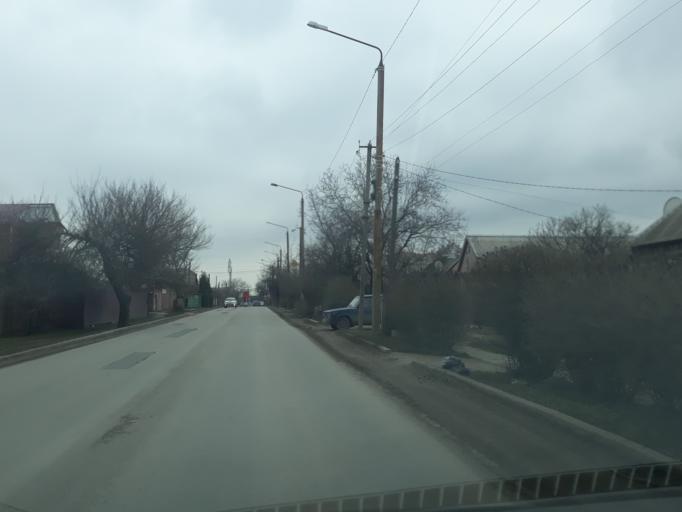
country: RU
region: Rostov
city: Taganrog
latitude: 47.2653
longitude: 38.8925
